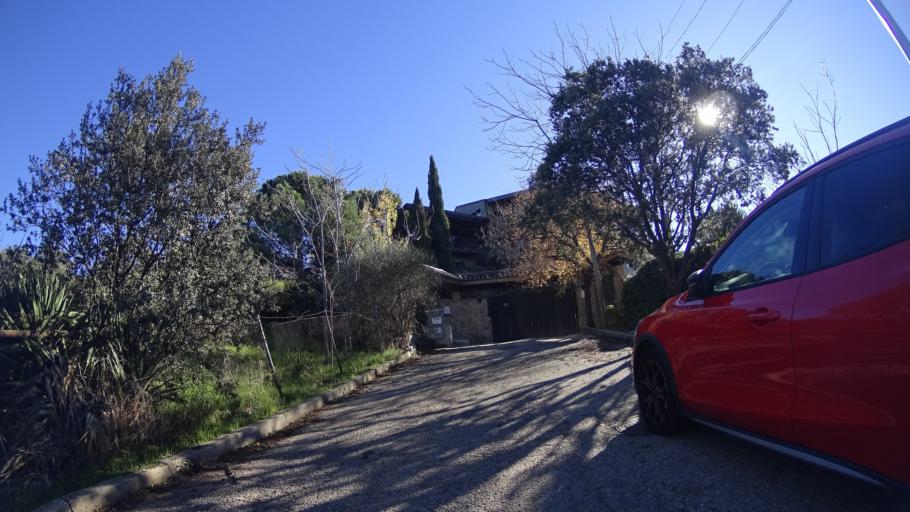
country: ES
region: Madrid
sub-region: Provincia de Madrid
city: Torrelodones
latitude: 40.5868
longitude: -3.9511
